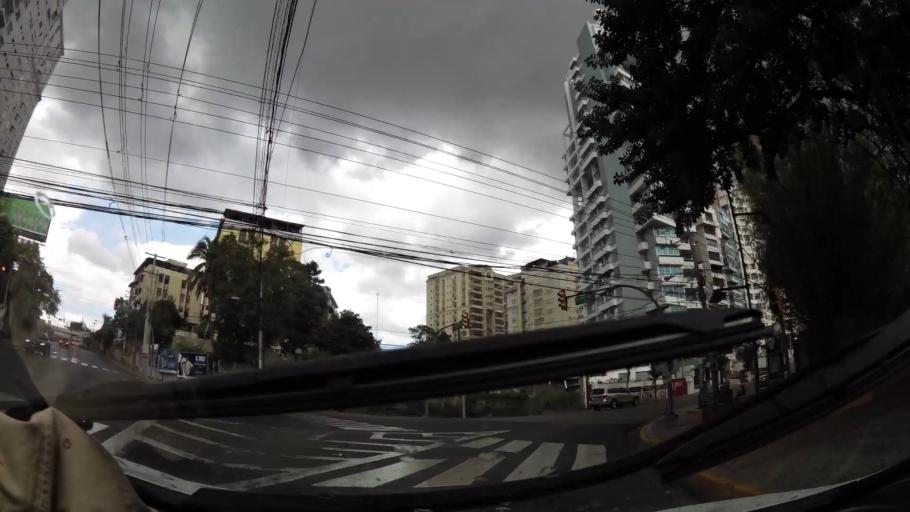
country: DO
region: Nacional
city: La Julia
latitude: 18.4672
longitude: -69.9216
